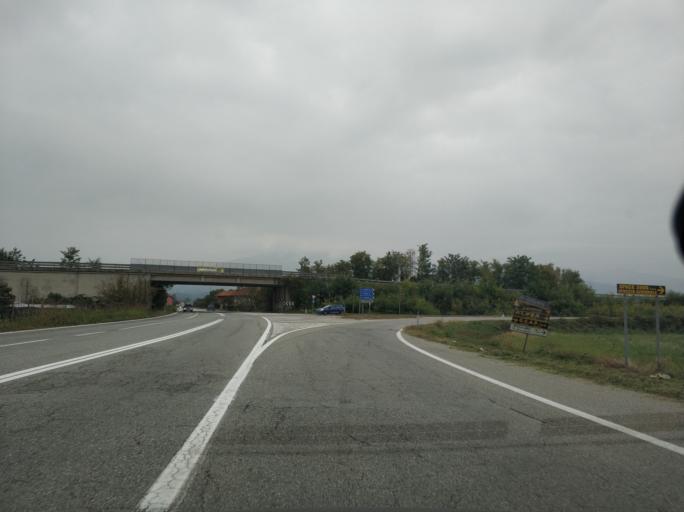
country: IT
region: Piedmont
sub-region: Provincia di Torino
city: Castellamonte
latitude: 45.3645
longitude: 7.7255
